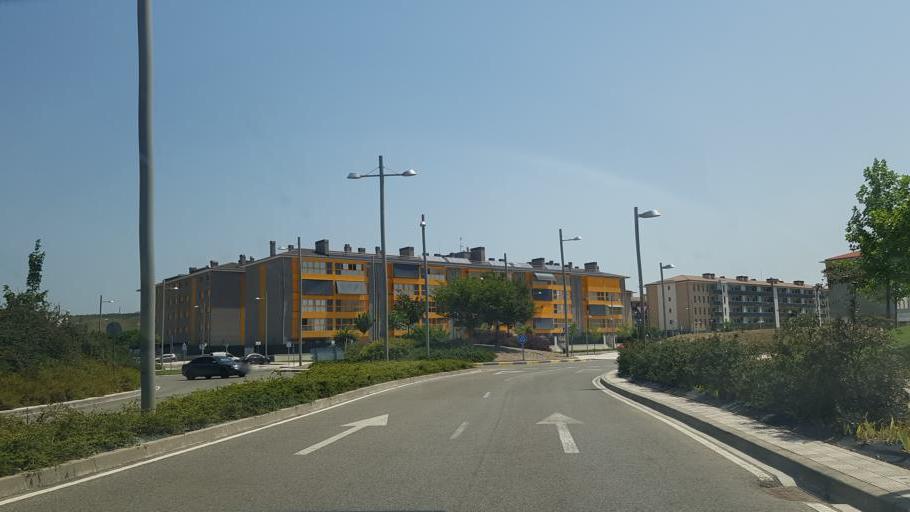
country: ES
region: Navarre
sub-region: Provincia de Navarra
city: Burlata
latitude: 42.7958
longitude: -1.6191
